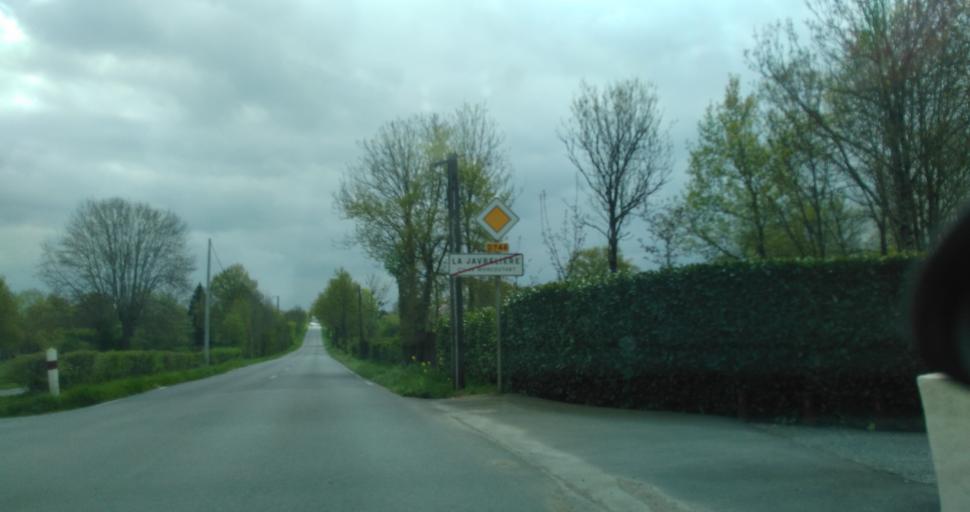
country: FR
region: Poitou-Charentes
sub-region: Departement des Deux-Sevres
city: Moncoutant
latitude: 46.7357
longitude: -0.6013
